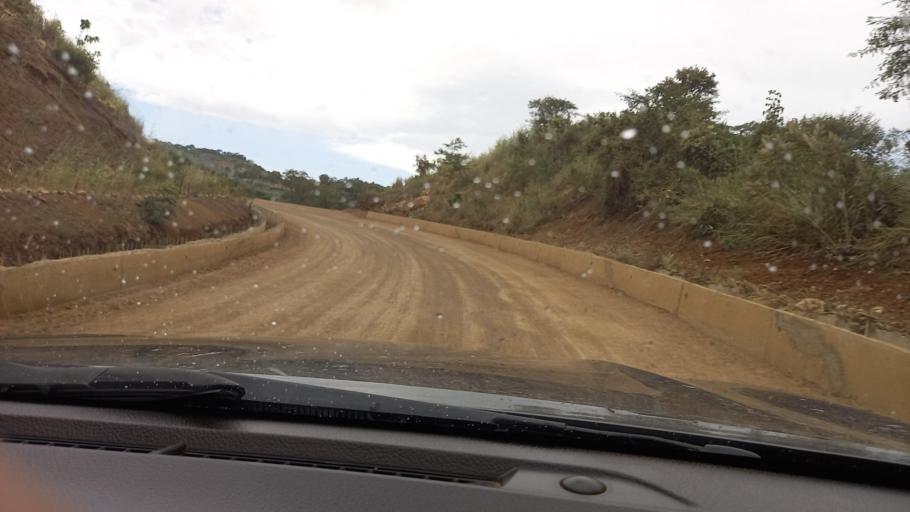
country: ET
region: Southern Nations, Nationalities, and People's Region
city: Mizan Teferi
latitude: 6.1910
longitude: 35.6743
